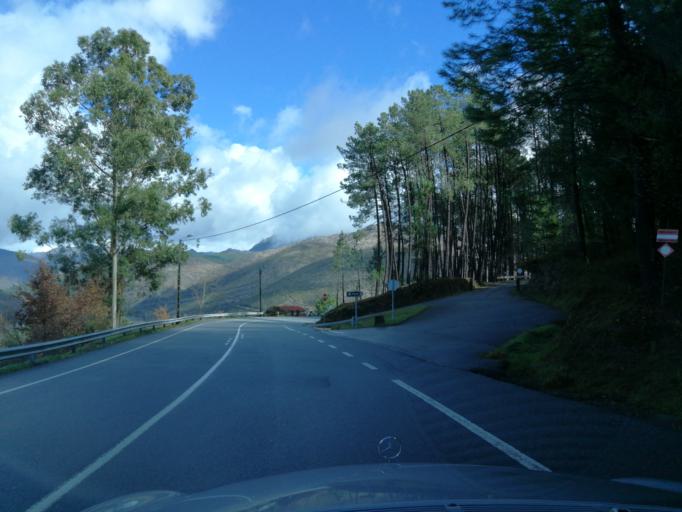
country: ES
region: Galicia
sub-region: Provincia de Ourense
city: Entrimo
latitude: 41.8698
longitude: -8.1948
